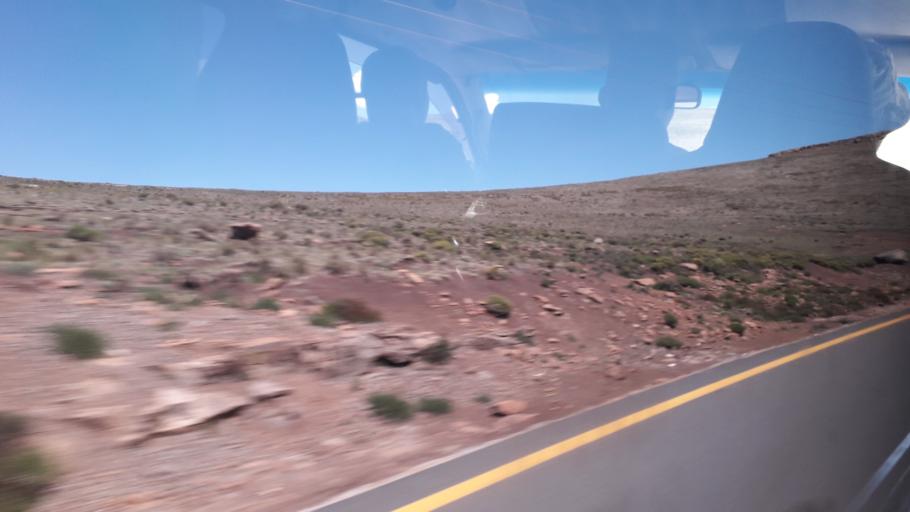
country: LS
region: Mokhotlong
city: Mokhotlong
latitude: -29.0634
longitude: 28.8502
